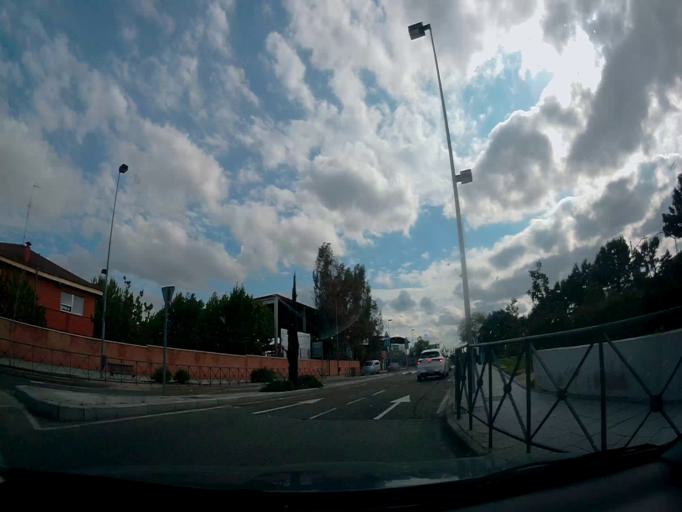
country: ES
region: Madrid
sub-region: Provincia de Madrid
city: Alcorcon
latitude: 40.3457
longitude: -3.8377
